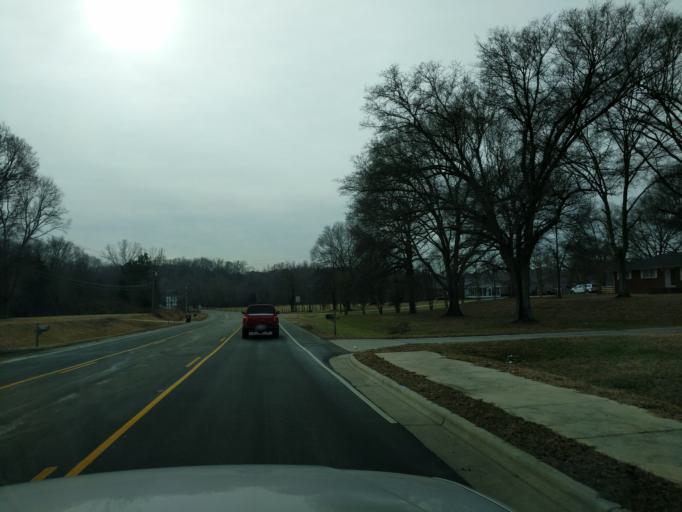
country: US
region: North Carolina
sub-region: Mecklenburg County
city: Huntersville
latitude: 35.3312
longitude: -80.9115
